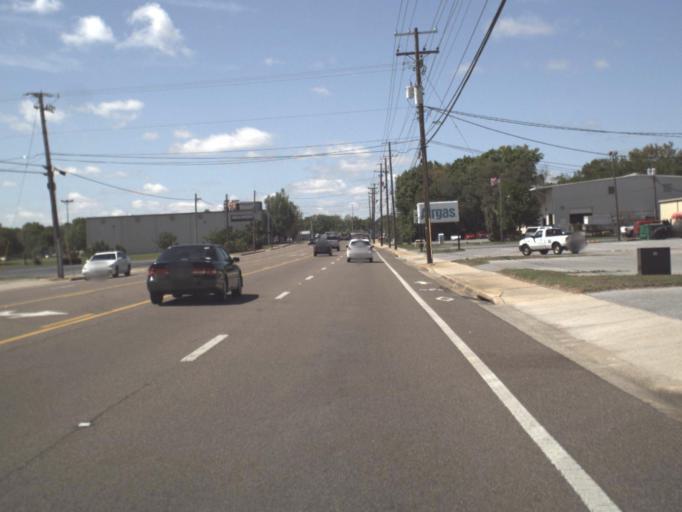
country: US
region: Florida
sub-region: Escambia County
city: Brent
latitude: 30.4560
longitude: -87.2368
